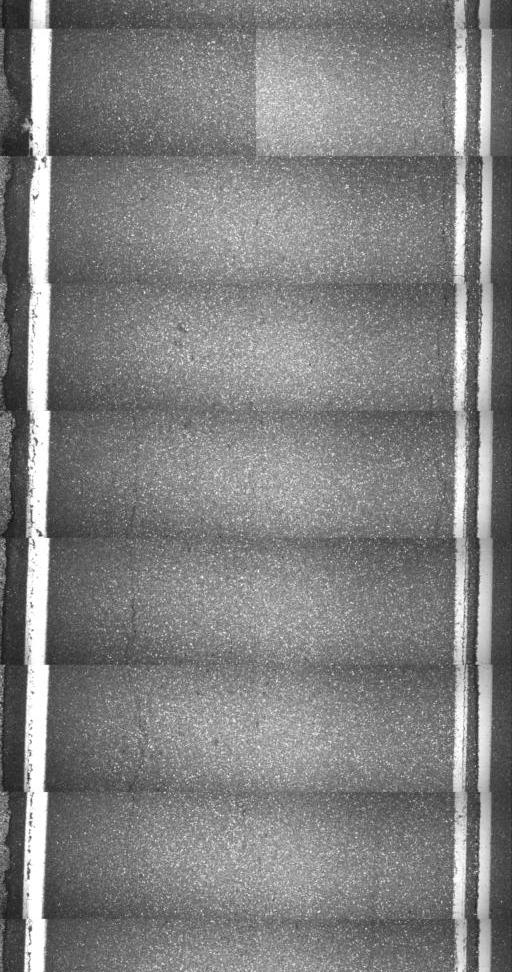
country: US
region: Vermont
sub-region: Orange County
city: Randolph
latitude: 43.8346
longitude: -72.7934
